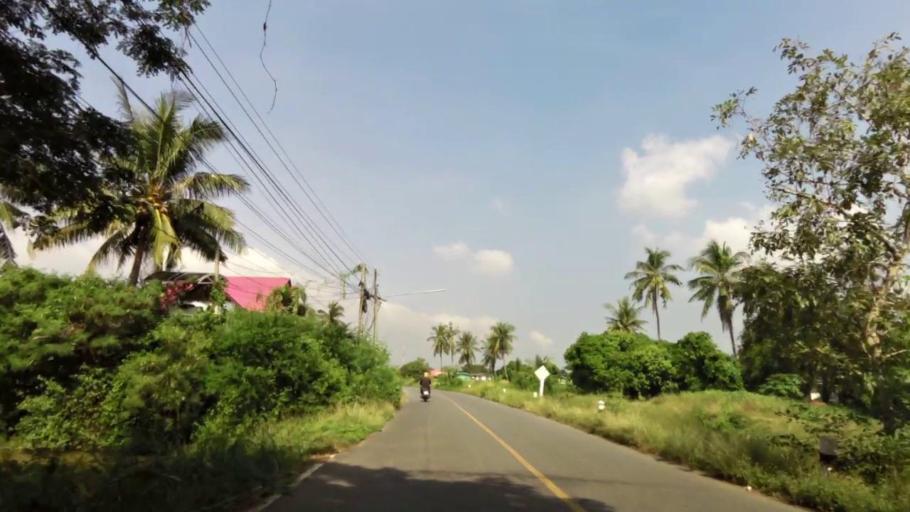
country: TH
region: Ang Thong
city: Ang Thong
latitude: 14.5989
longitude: 100.4023
